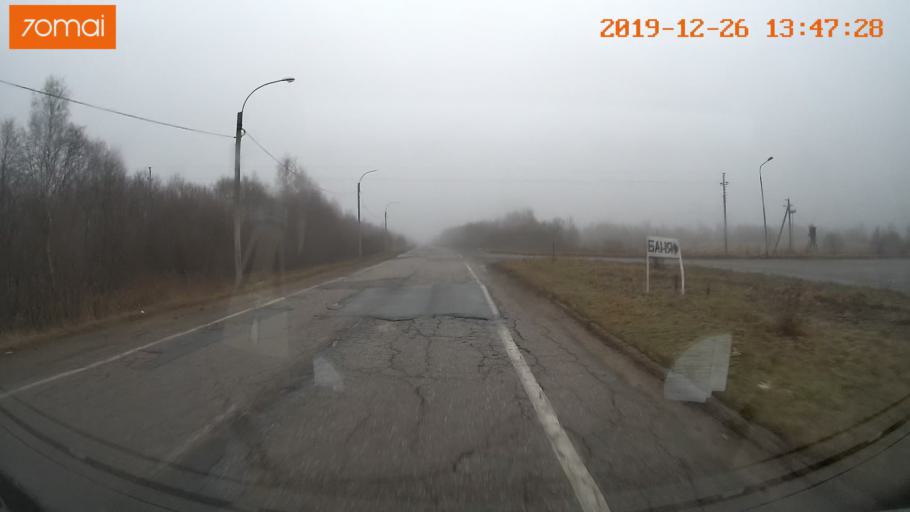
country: RU
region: Vologda
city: Sheksna
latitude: 58.6846
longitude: 38.5345
